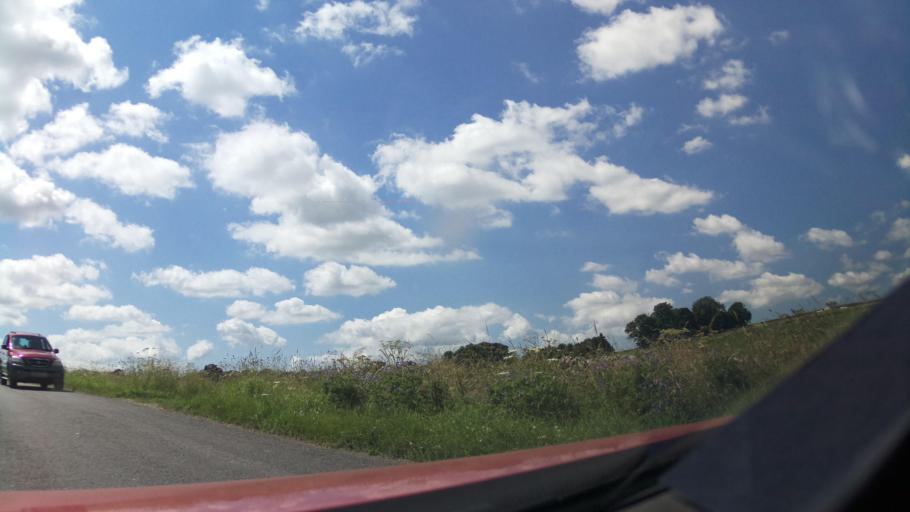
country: GB
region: England
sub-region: Derbyshire
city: Tideswell
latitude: 53.1855
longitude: -1.7801
